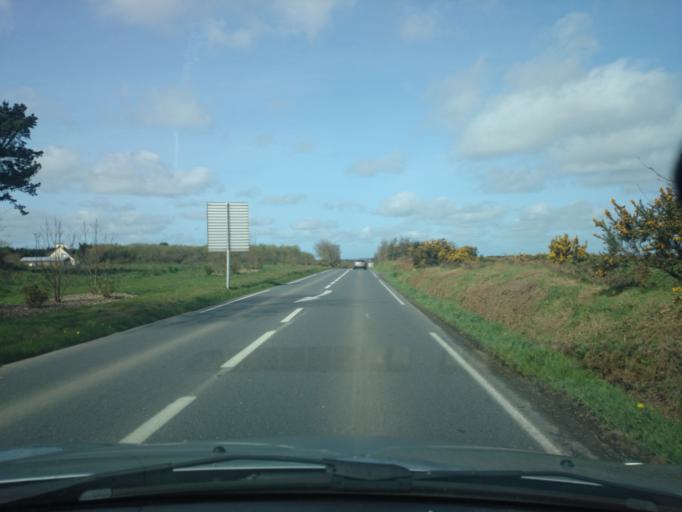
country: FR
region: Brittany
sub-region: Departement du Finistere
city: Guipavas
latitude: 48.4418
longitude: -4.4250
